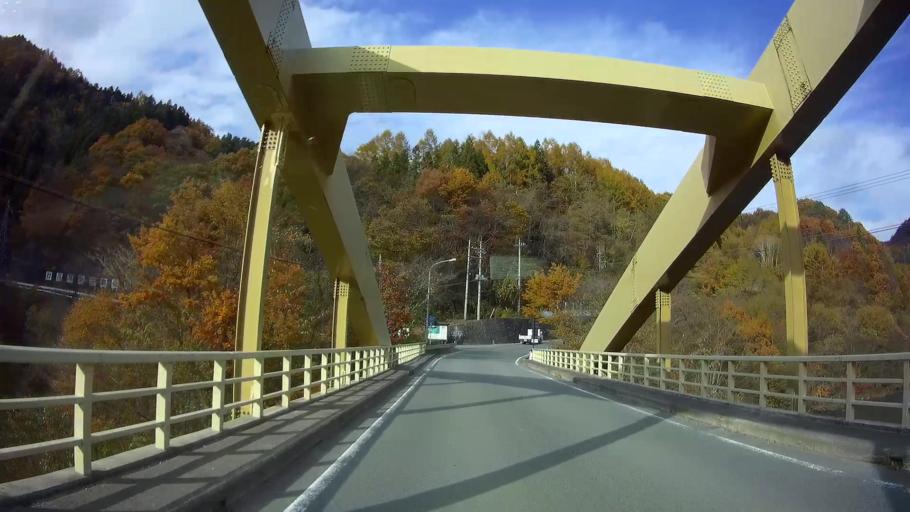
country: JP
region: Gunma
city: Nakanojomachi
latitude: 36.6512
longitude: 138.6515
